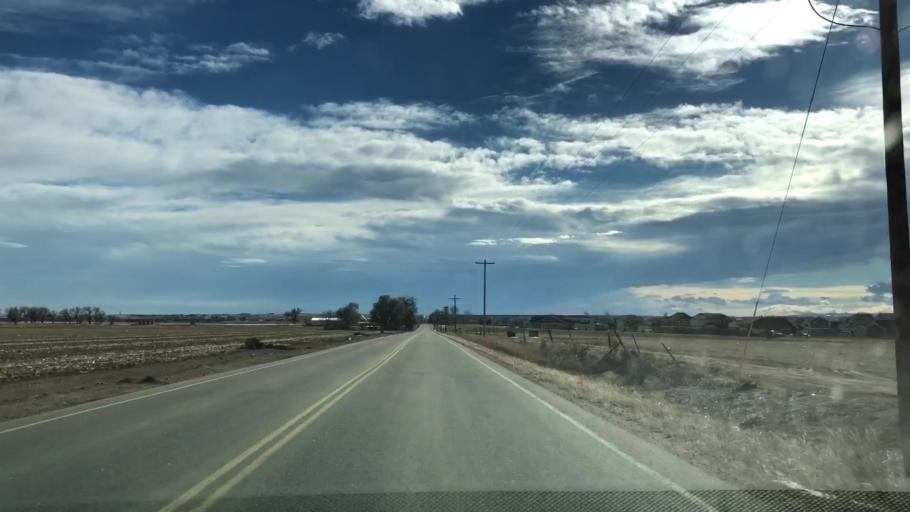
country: US
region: Colorado
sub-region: Weld County
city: Windsor
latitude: 40.5172
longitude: -104.9443
